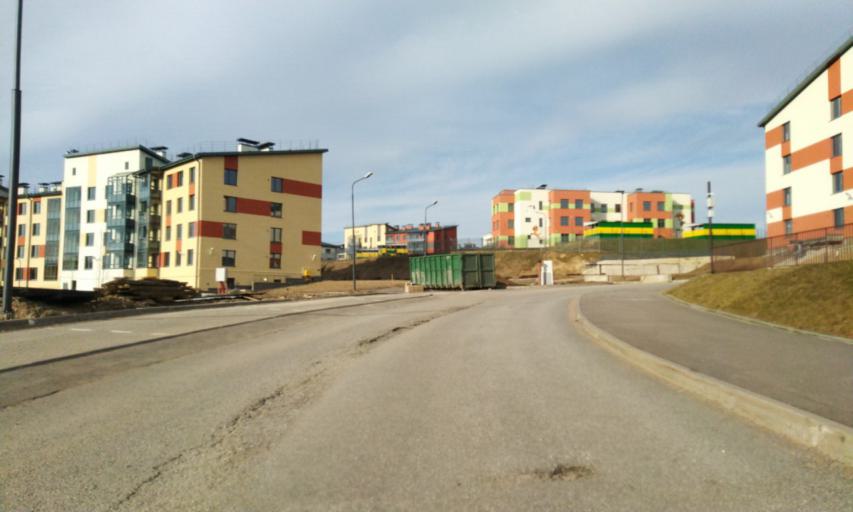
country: RU
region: Leningrad
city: Bugry
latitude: 60.1208
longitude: 30.4217
